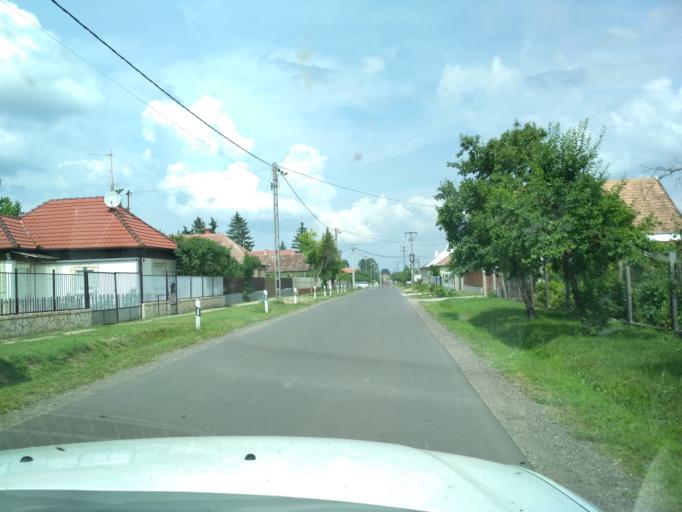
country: HU
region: Pest
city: Tapioszentmarton
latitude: 47.3330
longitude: 19.7569
